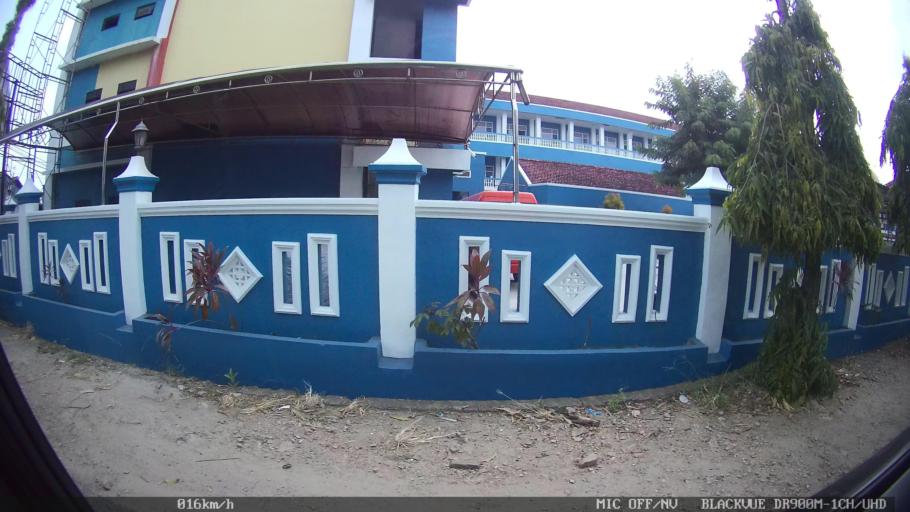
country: ID
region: Lampung
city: Pringsewu
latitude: -5.3478
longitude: 104.9724
